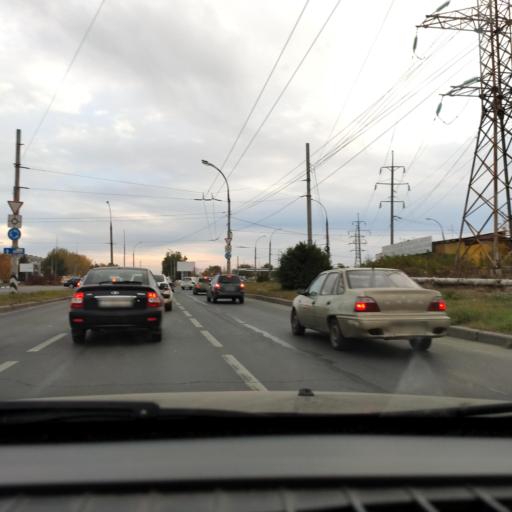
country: RU
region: Samara
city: Tol'yatti
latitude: 53.5318
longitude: 49.2616
